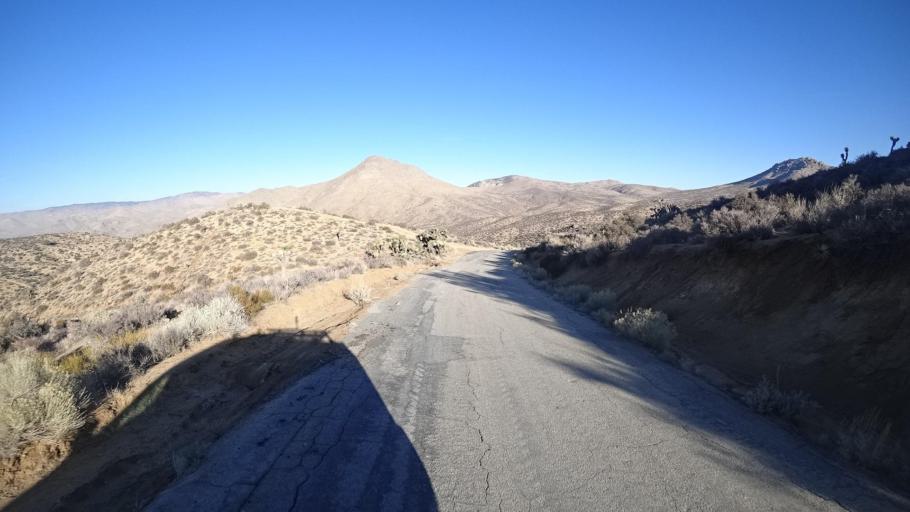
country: US
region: California
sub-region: Kern County
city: Weldon
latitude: 35.4508
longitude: -118.2234
